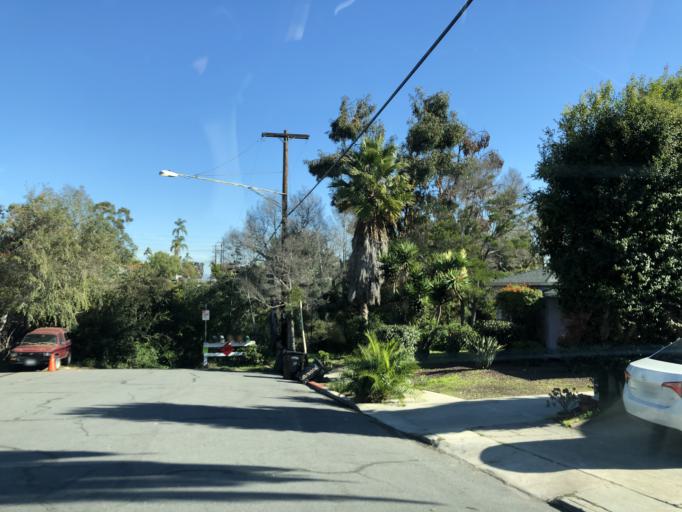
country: US
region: California
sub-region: San Diego County
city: San Diego
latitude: 32.7356
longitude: -117.1277
